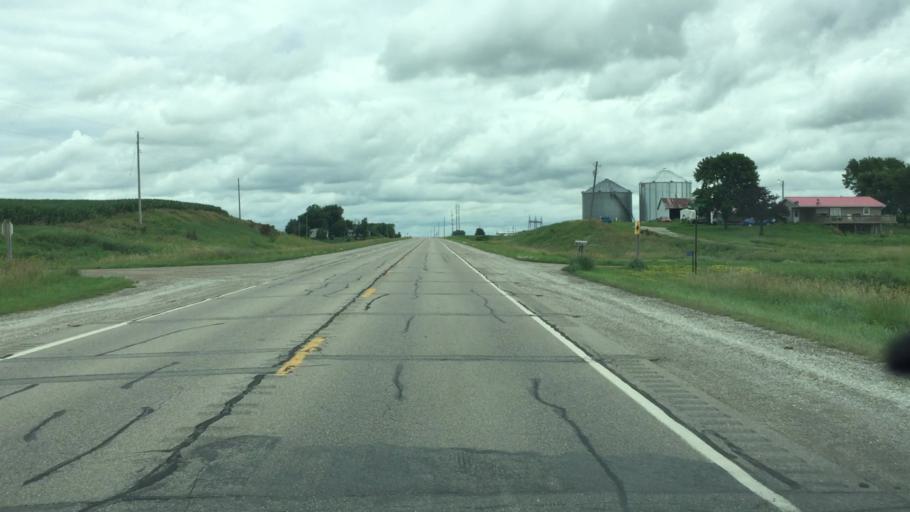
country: US
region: Iowa
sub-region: Jasper County
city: Monroe
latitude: 41.5659
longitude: -93.0970
